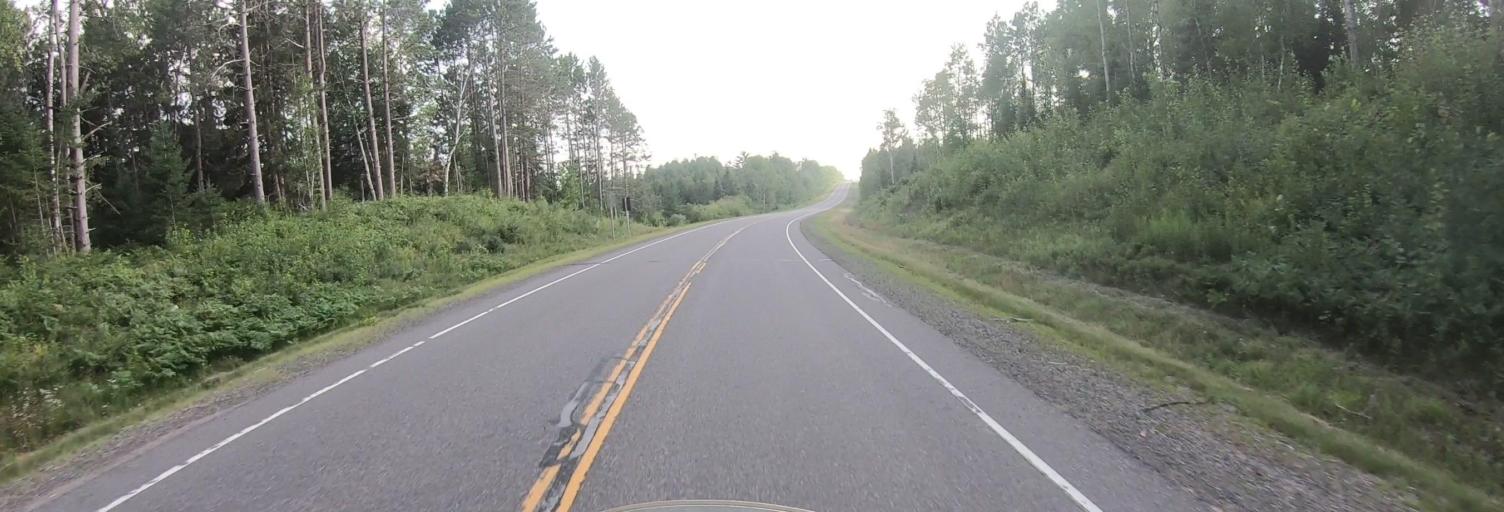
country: US
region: Wisconsin
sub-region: Sawyer County
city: Little Round Lake
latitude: 46.0859
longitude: -91.0117
